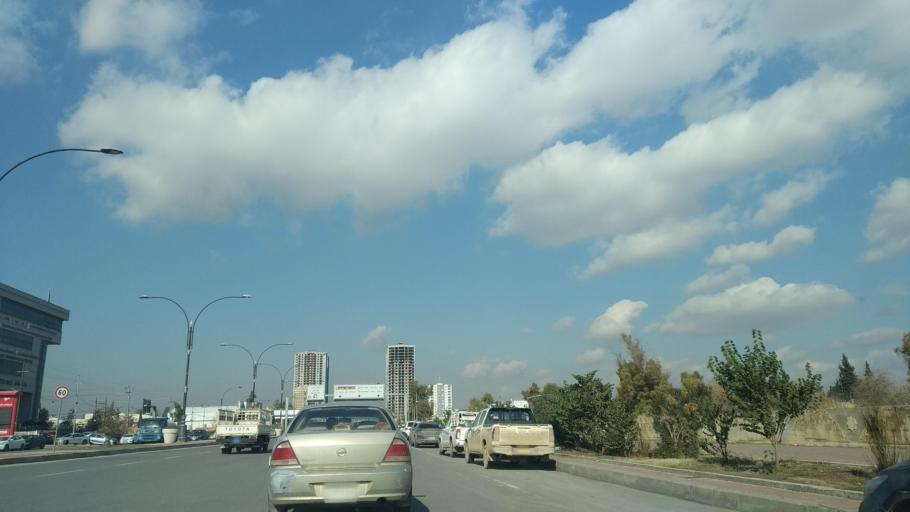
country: IQ
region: Arbil
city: Erbil
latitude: 36.1400
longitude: 44.0210
